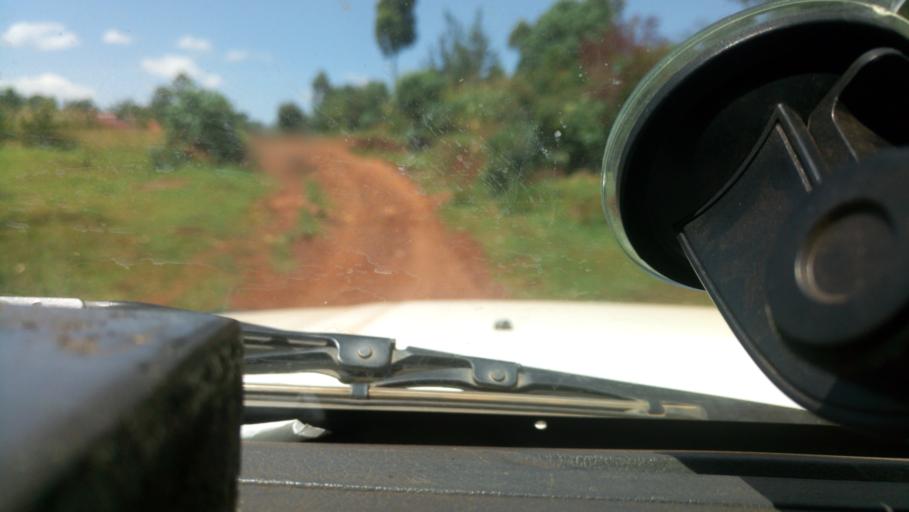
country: KE
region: Kisii
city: Ogembo
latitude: -0.8610
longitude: 34.7028
